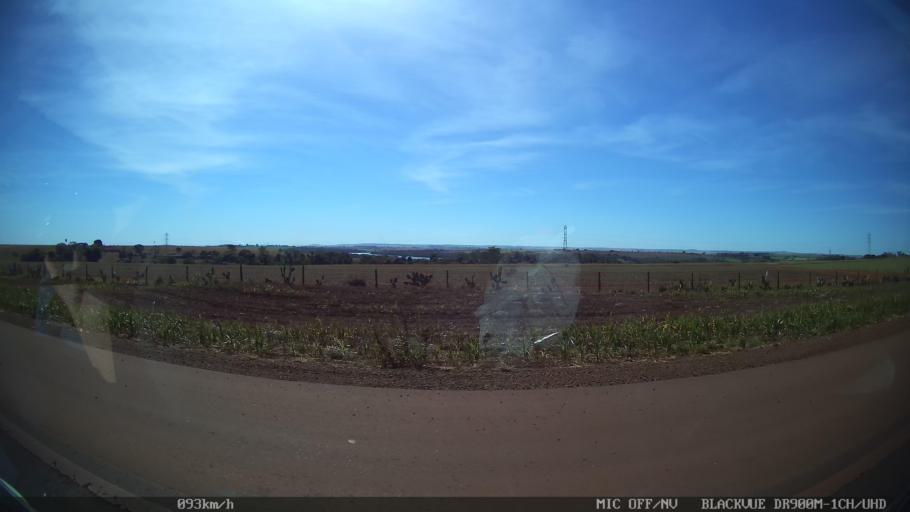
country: BR
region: Sao Paulo
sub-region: Sao Joaquim Da Barra
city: Sao Joaquim da Barra
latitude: -20.5212
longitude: -47.8613
